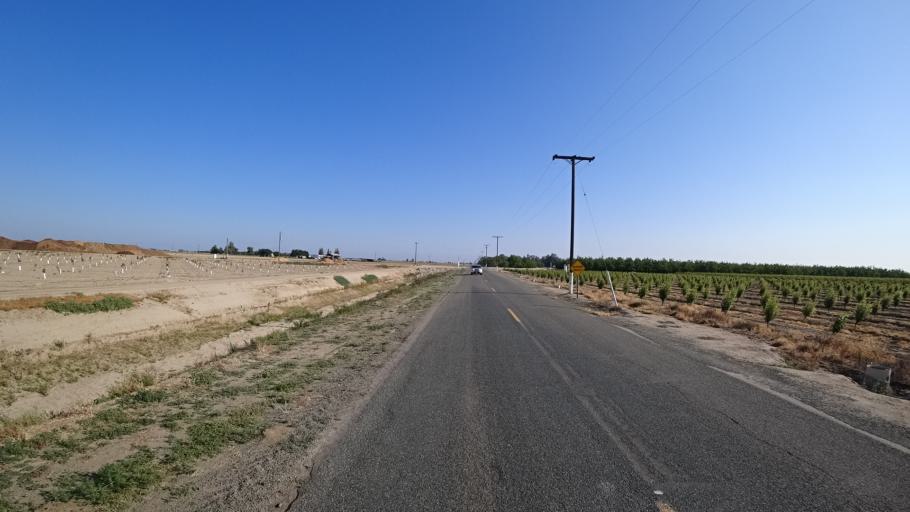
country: US
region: California
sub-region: Kings County
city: Home Garden
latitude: 36.2932
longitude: -119.5652
